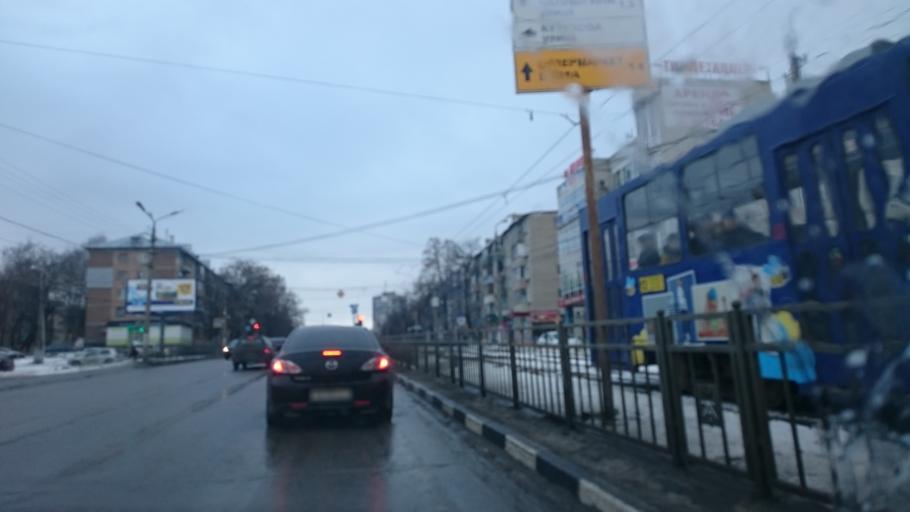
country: RU
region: Tula
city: Tula
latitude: 54.1958
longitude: 37.6818
